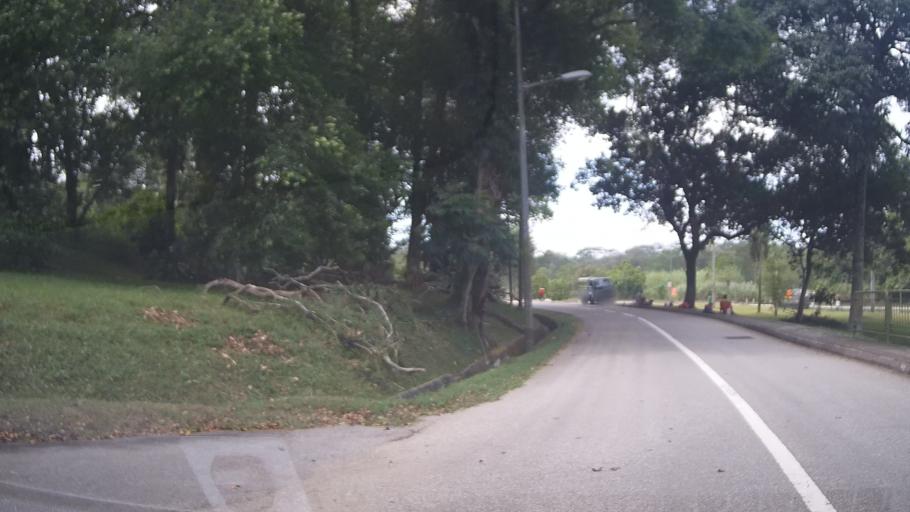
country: MY
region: Johor
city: Johor Bahru
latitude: 1.4035
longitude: 103.7021
